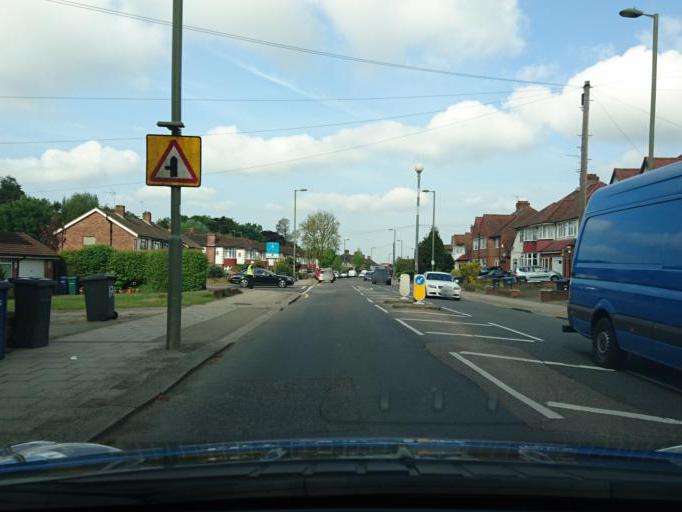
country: GB
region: England
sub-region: Greater London
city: Hadley Wood
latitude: 51.6452
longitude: -0.1491
